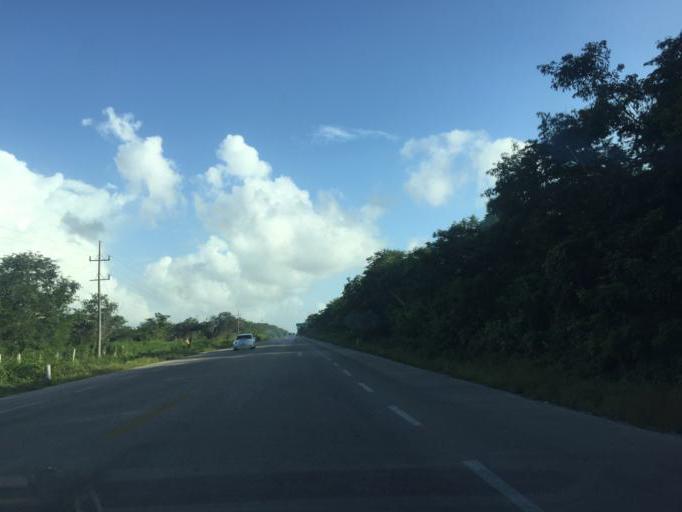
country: MX
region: Quintana Roo
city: Coba
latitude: 20.4904
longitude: -87.7034
